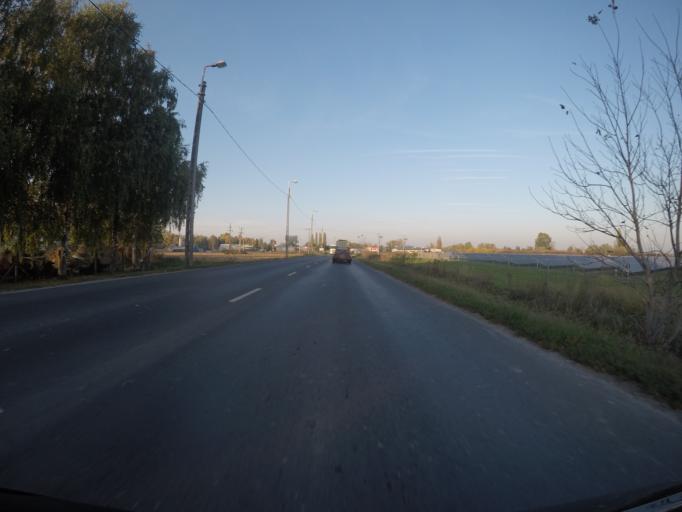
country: HU
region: Baranya
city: Szigetvar
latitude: 46.0450
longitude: 17.8175
